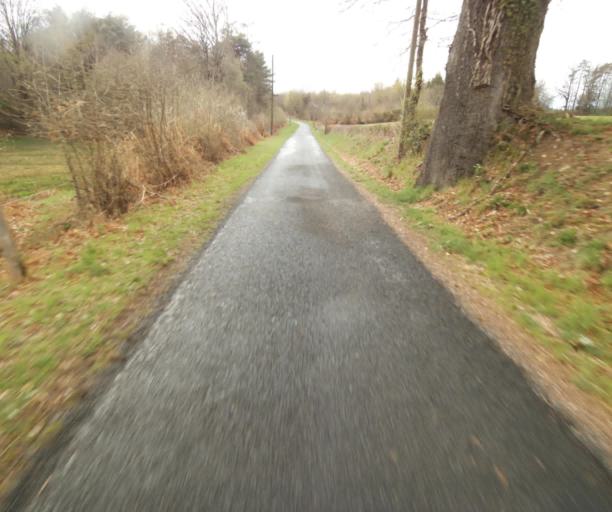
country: FR
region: Limousin
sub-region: Departement de la Correze
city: Saint-Privat
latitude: 45.2231
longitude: 2.0145
